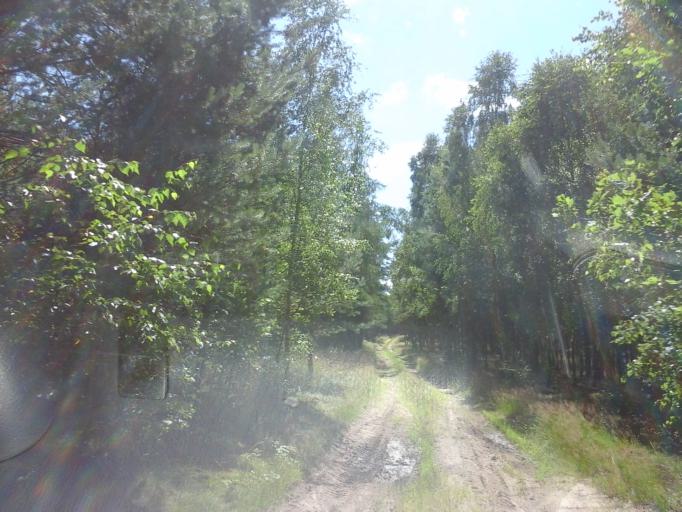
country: PL
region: West Pomeranian Voivodeship
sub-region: Powiat choszczenski
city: Drawno
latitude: 53.2699
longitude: 15.7281
